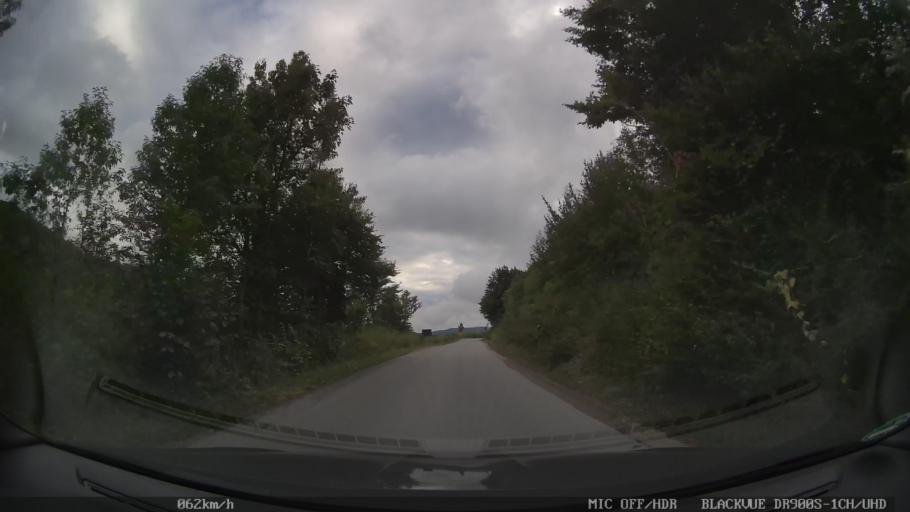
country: HR
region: Licko-Senjska
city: Jezerce
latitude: 44.9313
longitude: 15.6230
